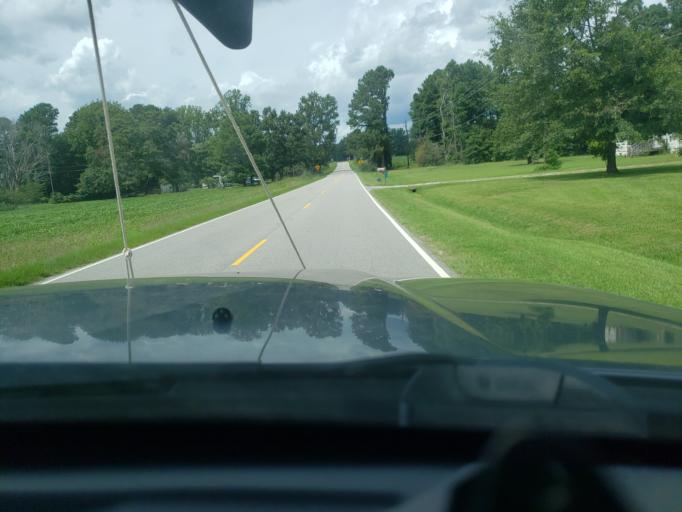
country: US
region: North Carolina
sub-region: Wake County
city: Rolesville
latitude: 35.8897
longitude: -78.4266
